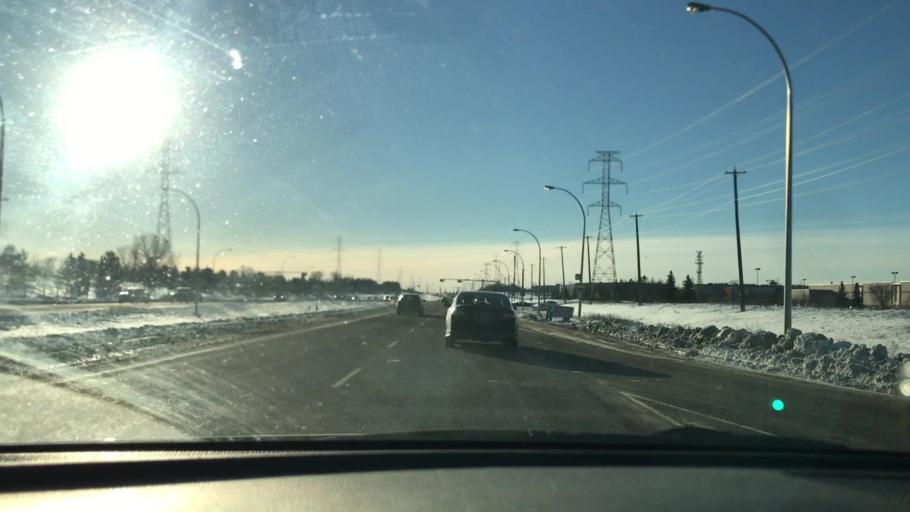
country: CA
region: Alberta
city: Edmonton
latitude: 53.4585
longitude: -113.4669
